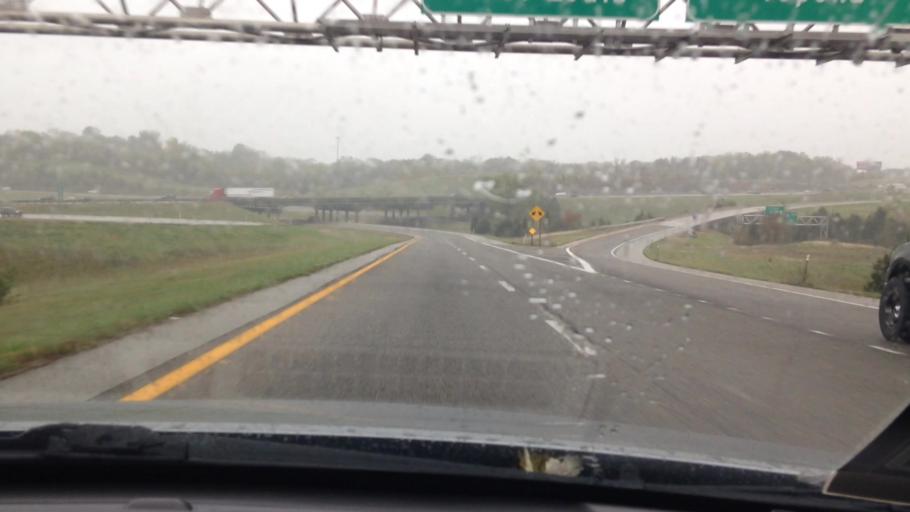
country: US
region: Kansas
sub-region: Wyandotte County
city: Edwardsville
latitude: 39.1093
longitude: -94.8130
